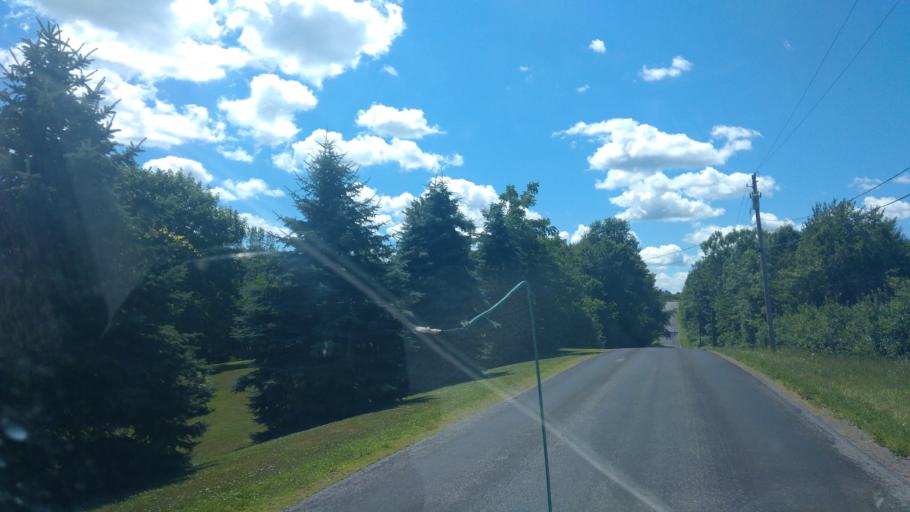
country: US
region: New York
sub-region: Wayne County
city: Lyons
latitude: 43.1480
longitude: -76.9733
